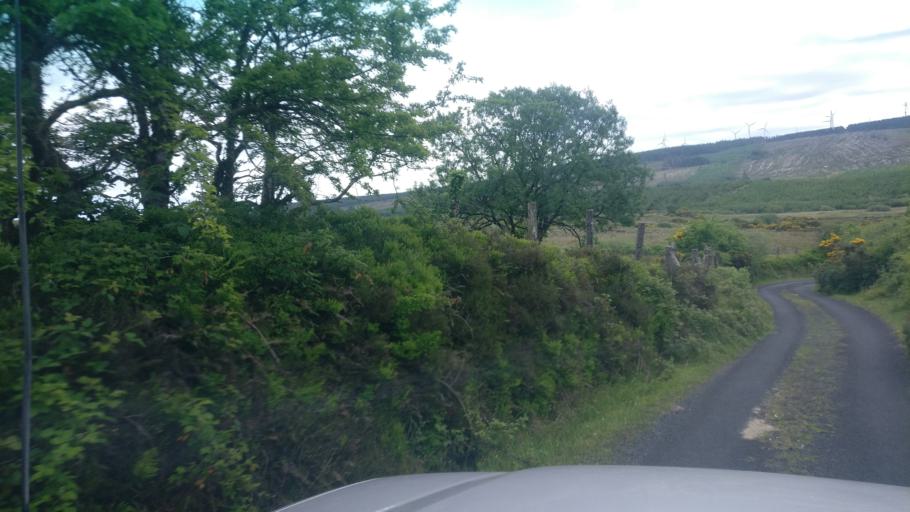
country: IE
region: Connaught
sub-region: County Galway
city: Loughrea
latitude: 53.1157
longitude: -8.6342
